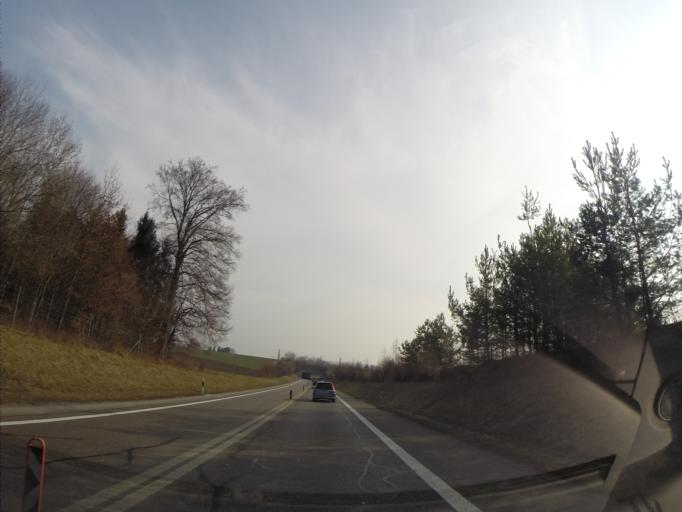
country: CH
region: Zurich
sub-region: Bezirk Andelfingen
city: Henggart
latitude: 47.5485
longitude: 8.6877
